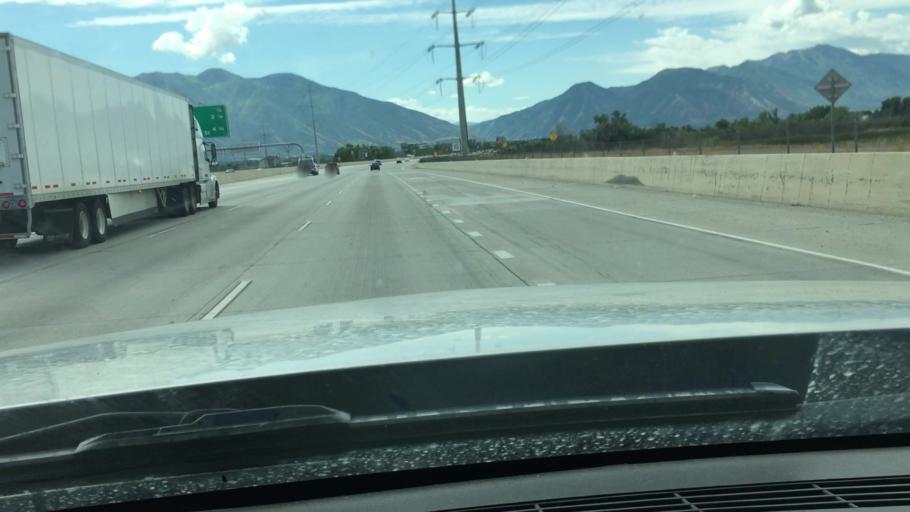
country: US
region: Utah
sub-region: Utah County
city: Provo
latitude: 40.1975
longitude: -111.6507
